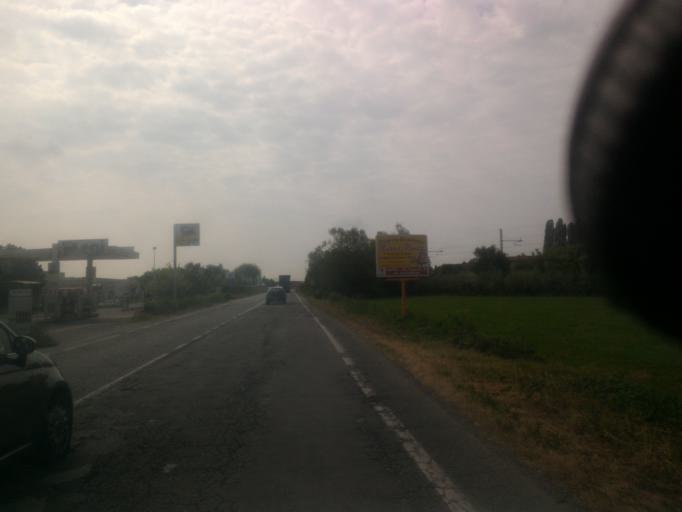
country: IT
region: Piedmont
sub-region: Provincia di Torino
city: Bricherasio
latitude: 44.8315
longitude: 7.3077
